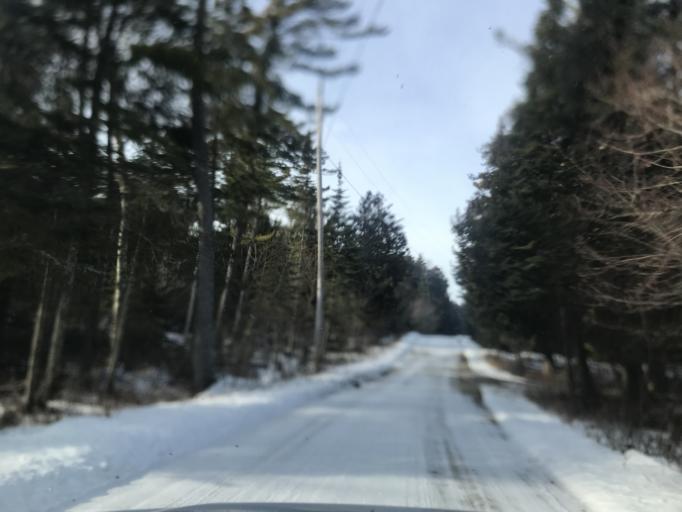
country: US
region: Wisconsin
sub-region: Door County
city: Sturgeon Bay
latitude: 45.1488
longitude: -87.0348
